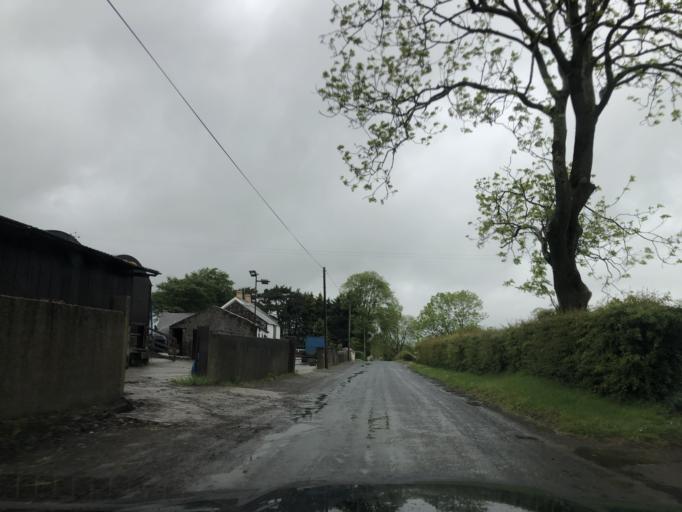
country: GB
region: Northern Ireland
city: Dunloy
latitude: 55.1129
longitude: -6.3472
